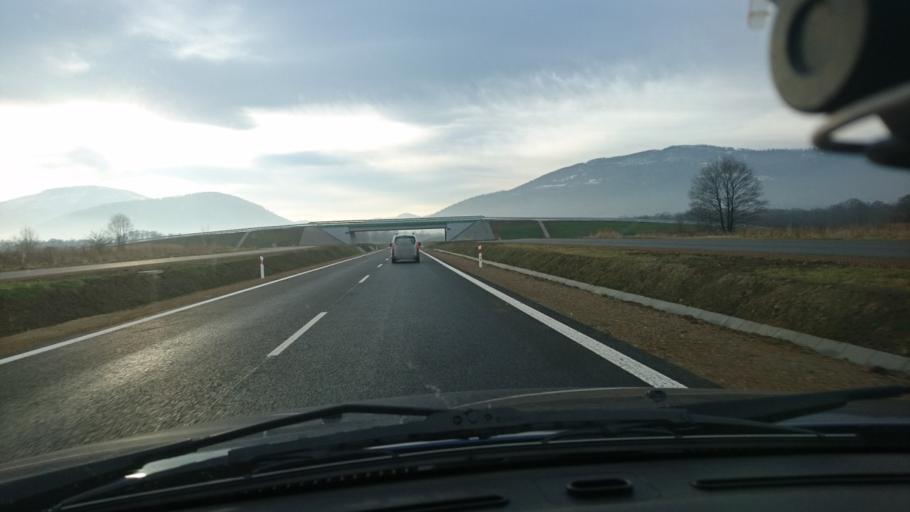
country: PL
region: Silesian Voivodeship
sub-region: Powiat bielski
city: Rybarzowice
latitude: 49.7406
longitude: 19.0858
